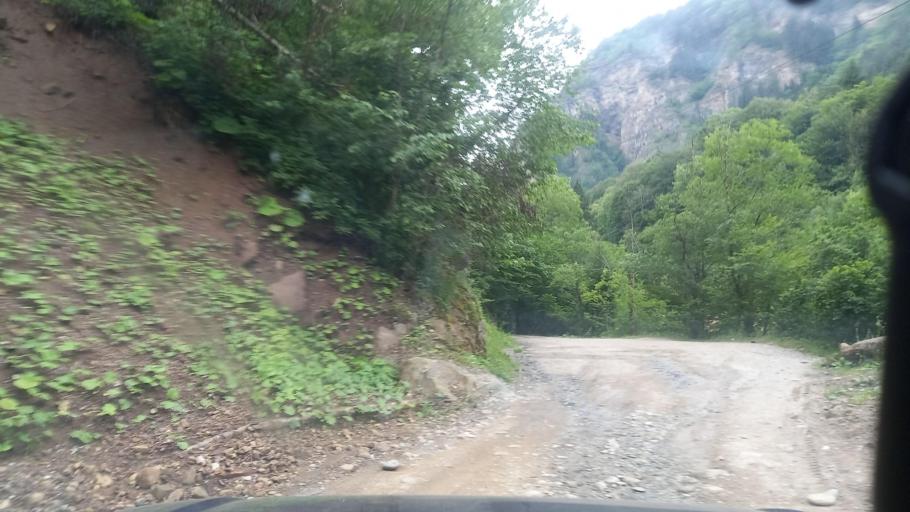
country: RU
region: Karachayevo-Cherkesiya
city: Kurdzhinovo
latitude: 43.8609
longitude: 40.9389
